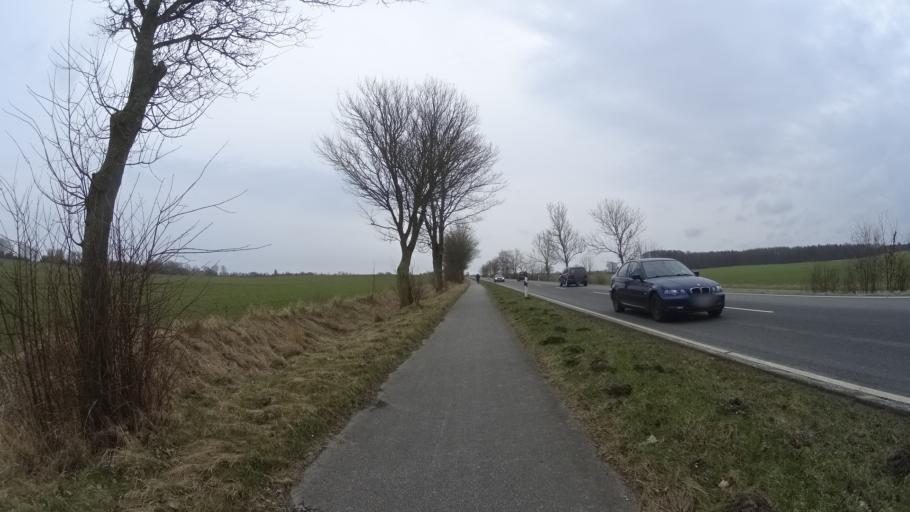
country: DE
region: Schleswig-Holstein
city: Stakendorf
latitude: 54.3811
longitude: 10.4482
